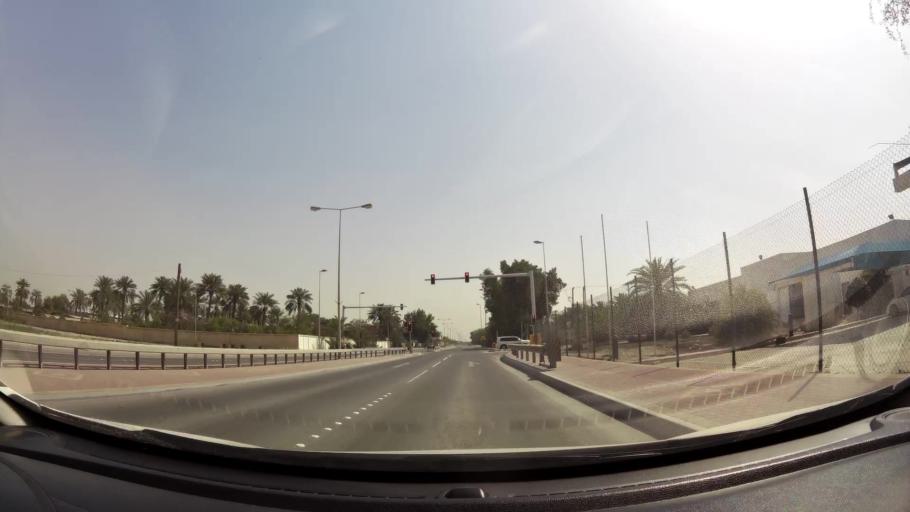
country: BH
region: Manama
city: Jidd Hafs
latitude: 26.2037
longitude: 50.4587
